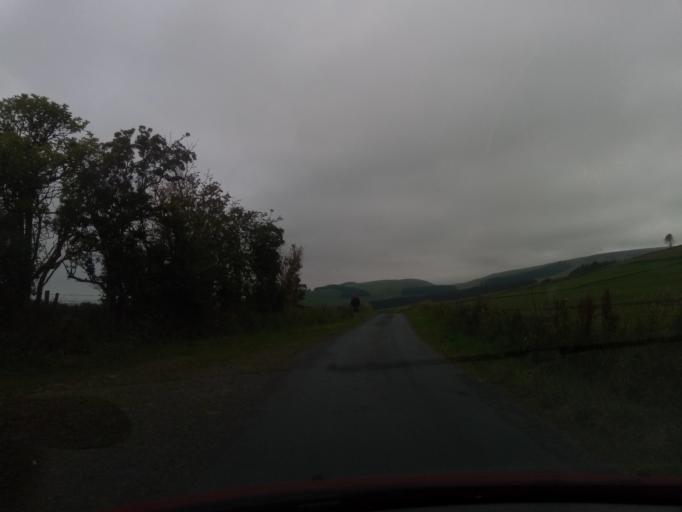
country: GB
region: Scotland
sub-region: The Scottish Borders
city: Galashiels
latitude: 55.6763
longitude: -2.8772
